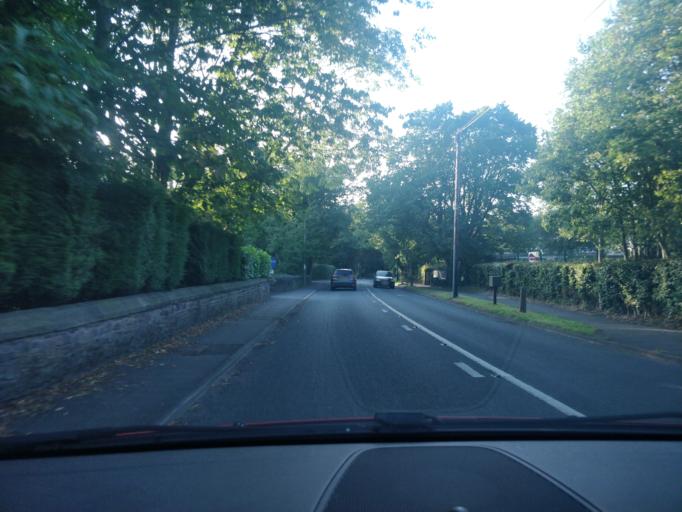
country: GB
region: England
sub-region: Lancashire
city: Parbold
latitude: 53.5929
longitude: -2.7643
